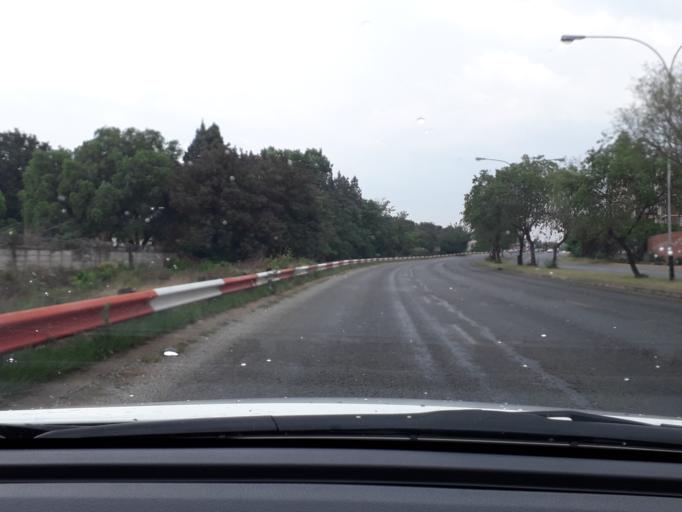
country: ZA
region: Gauteng
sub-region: City of Johannesburg Metropolitan Municipality
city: Johannesburg
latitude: -26.2358
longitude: 28.0273
